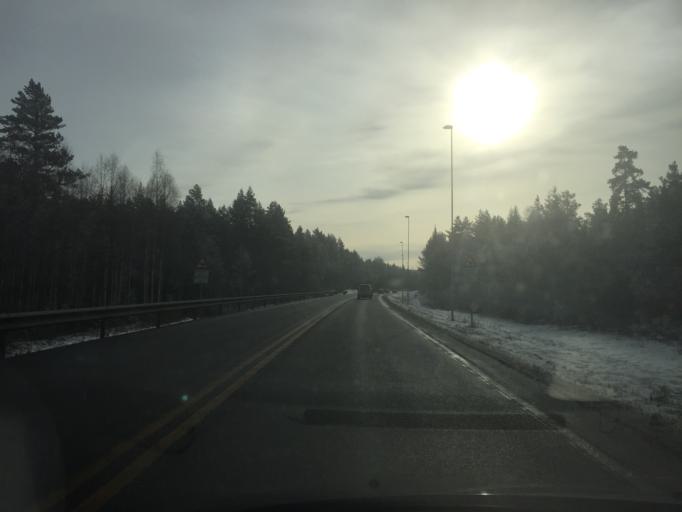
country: NO
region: Hedmark
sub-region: Loten
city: Loten
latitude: 60.7716
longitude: 11.3091
